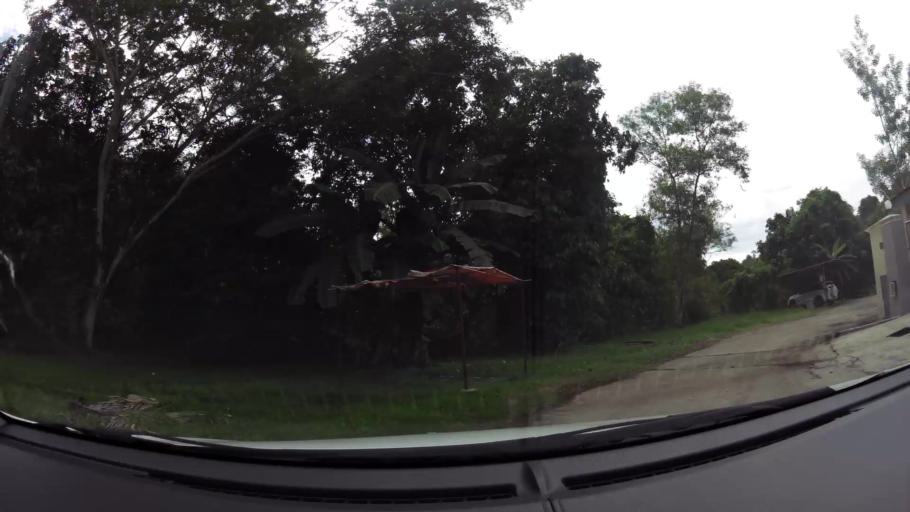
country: BN
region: Brunei and Muara
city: Bandar Seri Begawan
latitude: 4.8870
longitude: 114.8912
